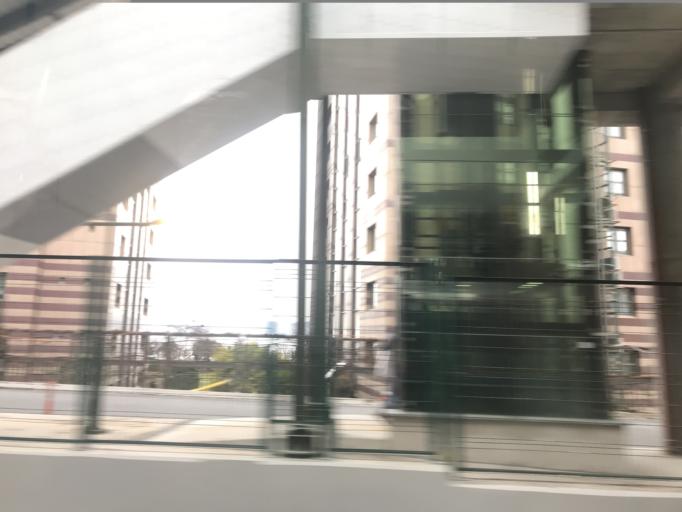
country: TR
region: Istanbul
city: Adalar
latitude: 40.8903
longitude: 29.1774
